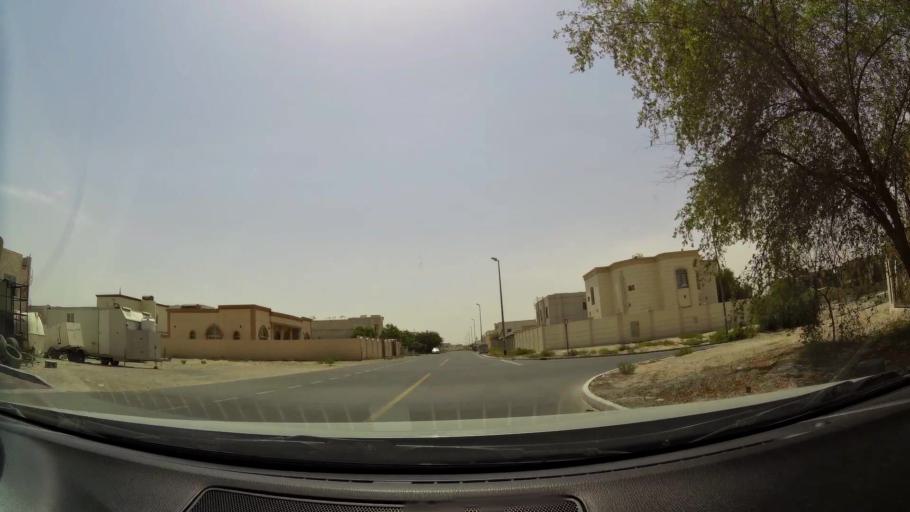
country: AE
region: Ash Shariqah
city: Sharjah
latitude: 25.1801
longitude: 55.4222
